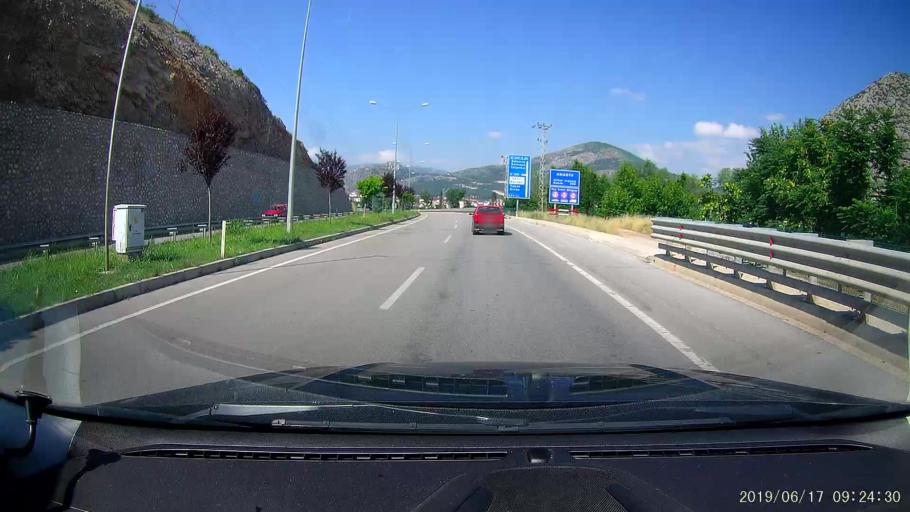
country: TR
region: Amasya
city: Amasya
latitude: 40.6719
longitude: 35.8563
